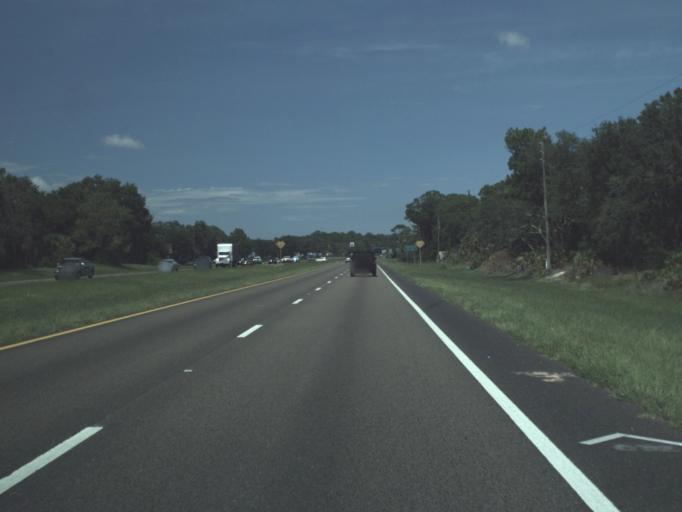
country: US
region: Florida
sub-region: Citrus County
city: Homosassa Springs
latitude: 28.7929
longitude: -82.5706
